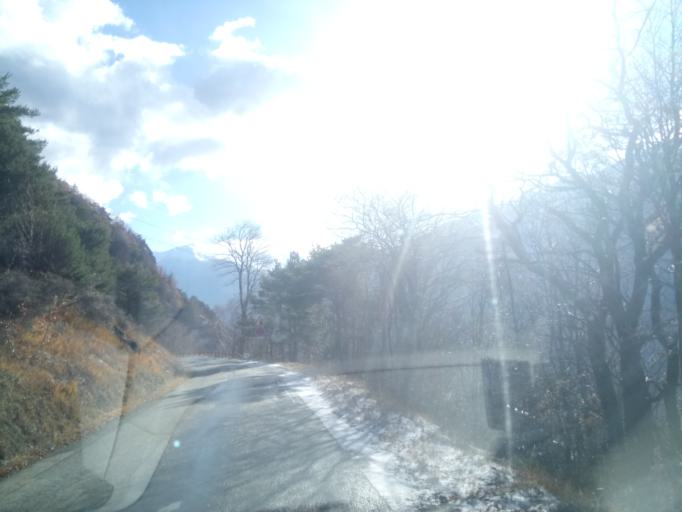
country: FR
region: Rhone-Alpes
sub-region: Departement de la Savoie
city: Villargondran
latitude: 45.2753
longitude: 6.3816
